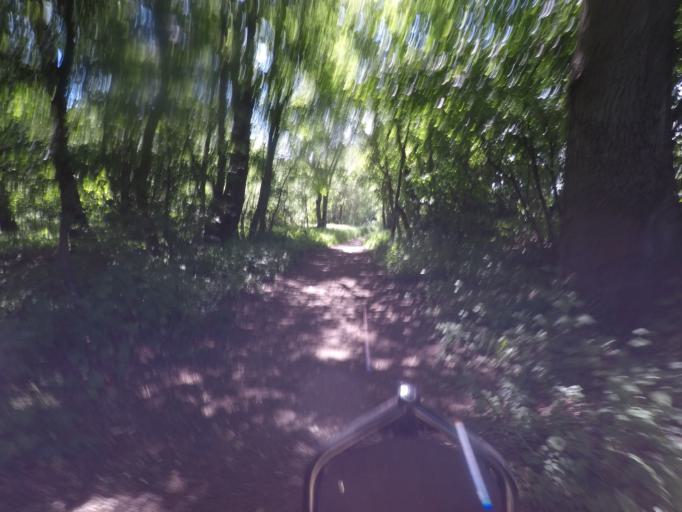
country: DE
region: Hamburg
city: Farmsen-Berne
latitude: 53.6169
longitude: 10.1688
